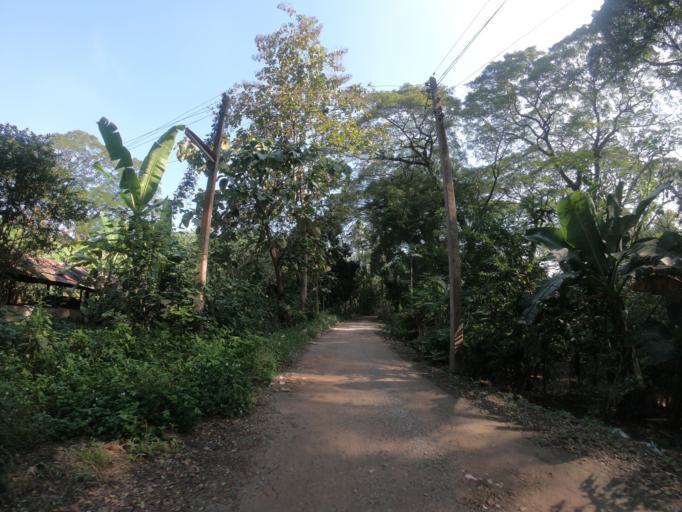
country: TH
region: Chiang Mai
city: Chiang Mai
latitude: 18.7381
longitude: 98.9875
